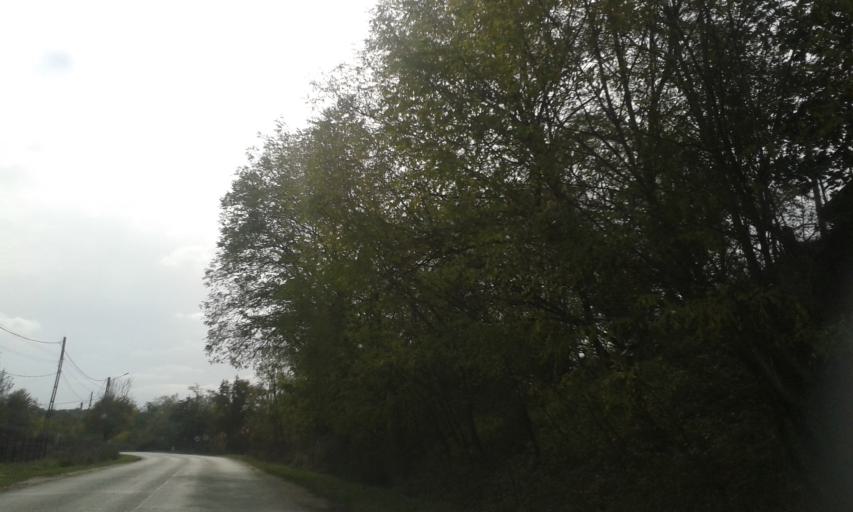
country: RO
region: Gorj
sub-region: Comuna Targu Carbunesti
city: Pojogeni
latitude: 44.9729
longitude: 23.5029
